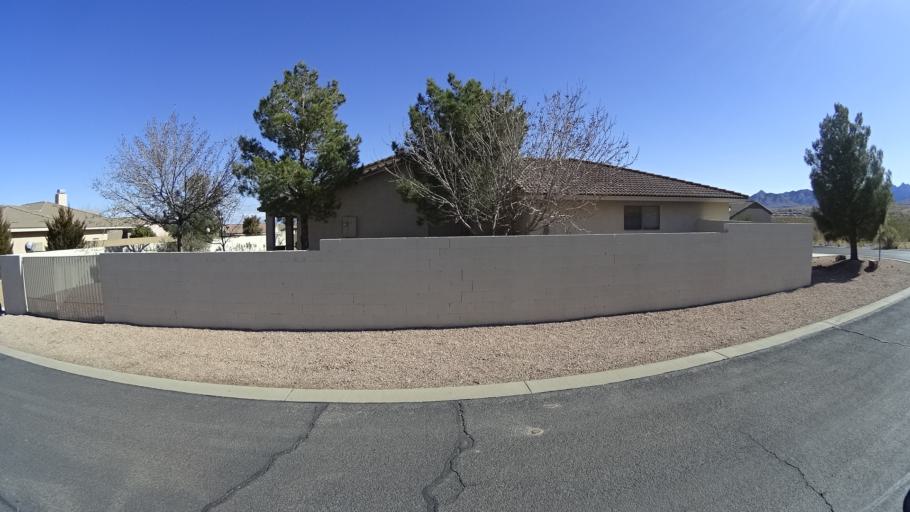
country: US
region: Arizona
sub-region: Mohave County
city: Kingman
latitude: 35.1871
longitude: -114.0259
